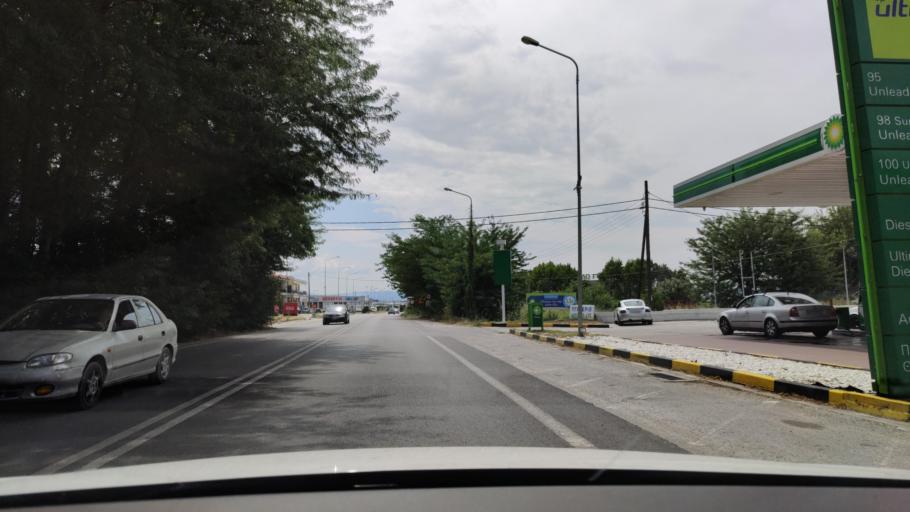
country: GR
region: Central Macedonia
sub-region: Nomos Serron
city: Serres
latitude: 41.0700
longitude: 23.5405
